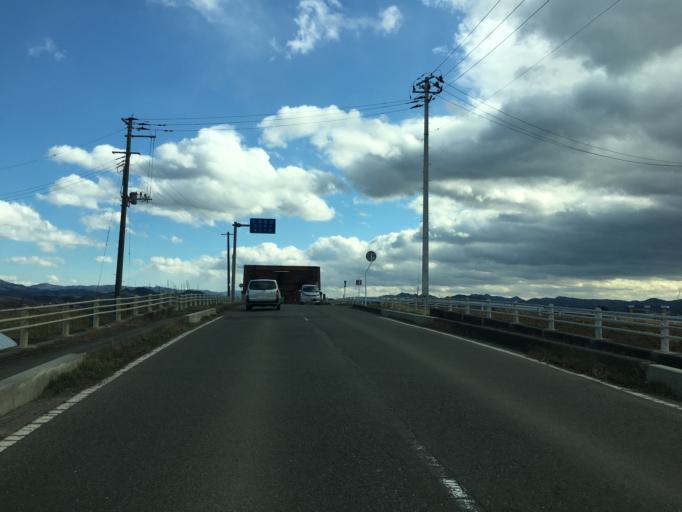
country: JP
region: Fukushima
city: Yanagawamachi-saiwaicho
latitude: 37.8640
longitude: 140.5688
